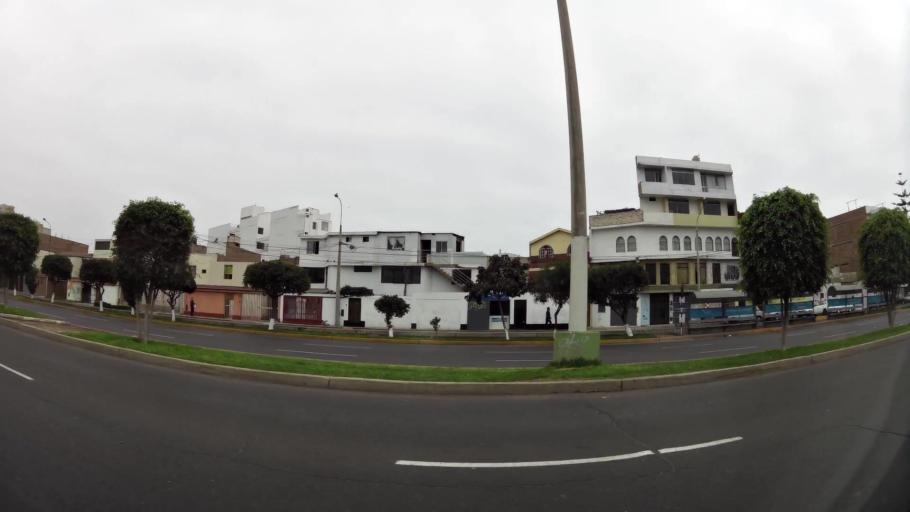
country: PE
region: Callao
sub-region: Callao
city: Callao
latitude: -12.0627
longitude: -77.1002
